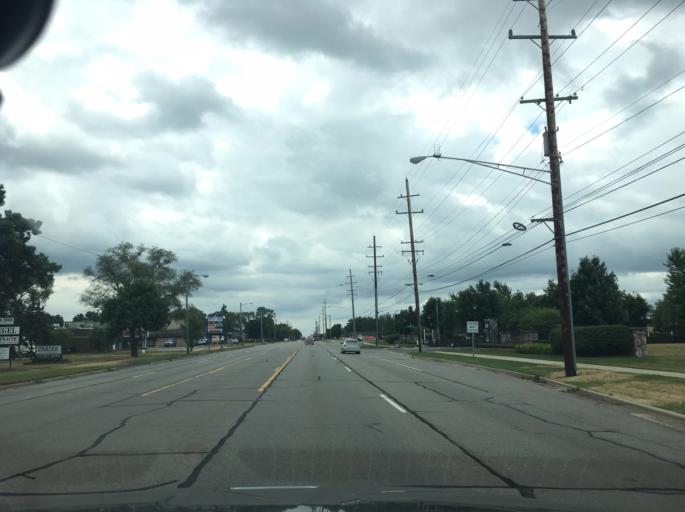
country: US
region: Michigan
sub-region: Macomb County
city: Shelby
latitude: 42.6608
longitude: -83.0336
